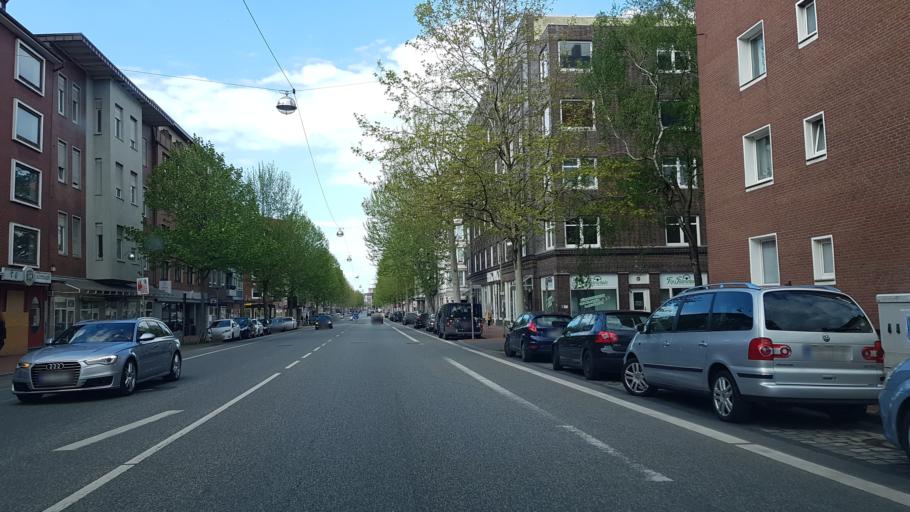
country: DE
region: Bremen
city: Bremerhaven
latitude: 53.5518
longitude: 8.5810
